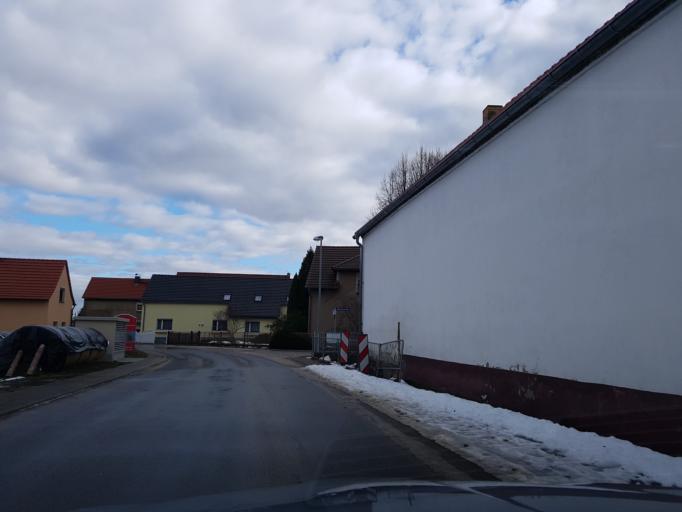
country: DE
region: Brandenburg
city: Merzdorf
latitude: 51.4016
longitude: 13.5330
